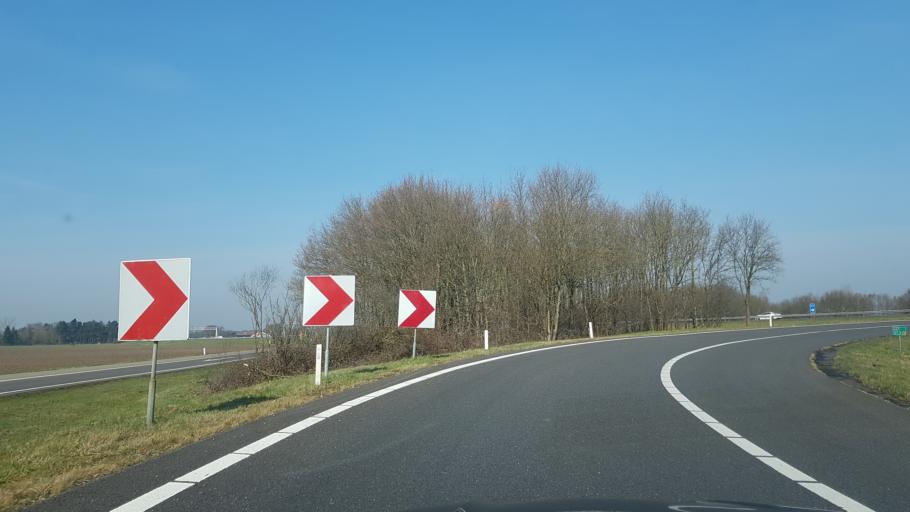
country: NL
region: North Brabant
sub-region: Gemeente Someren
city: Someren
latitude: 51.4214
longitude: 5.6960
